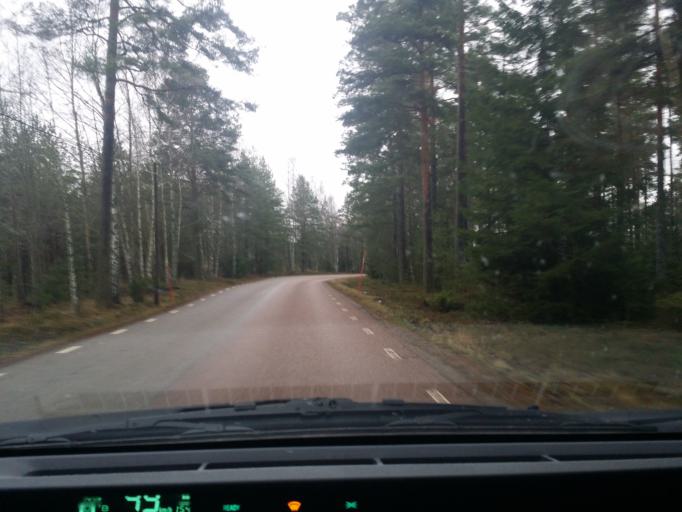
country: SE
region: Vaestmanland
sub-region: Sala Kommun
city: Sala
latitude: 59.8283
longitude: 16.5257
